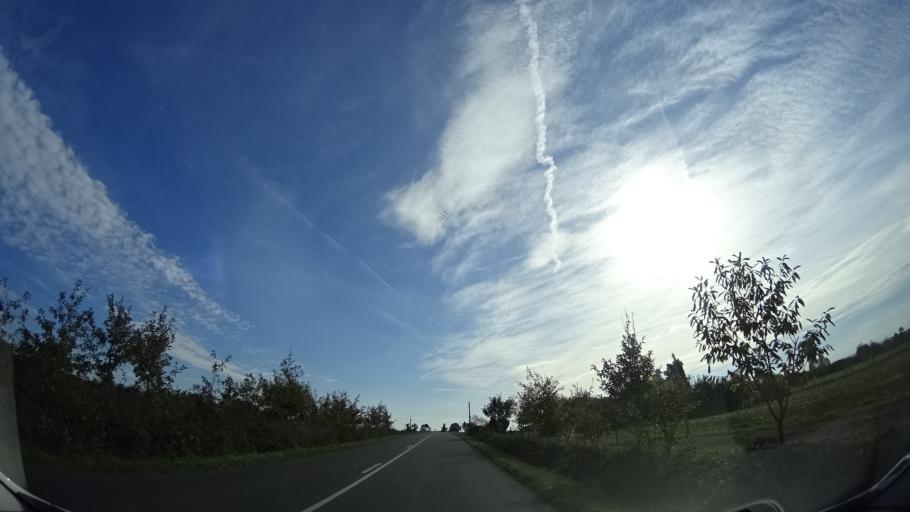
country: FR
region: Brittany
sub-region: Departement d'Ille-et-Vilaine
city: Bedee
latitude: 48.2007
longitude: -1.9398
